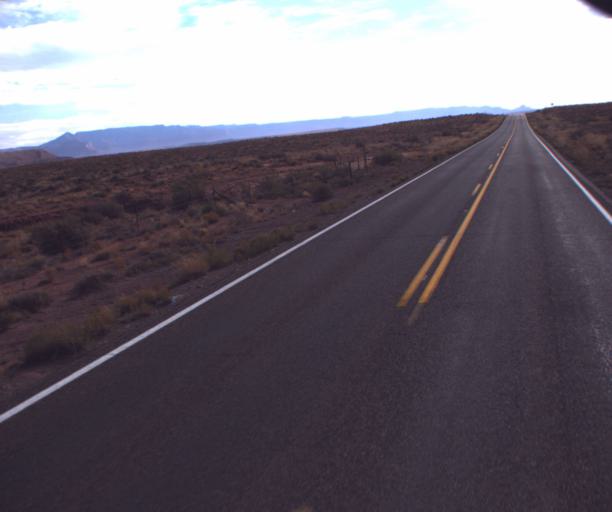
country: US
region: Arizona
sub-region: Apache County
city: Many Farms
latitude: 36.5354
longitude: -109.5146
